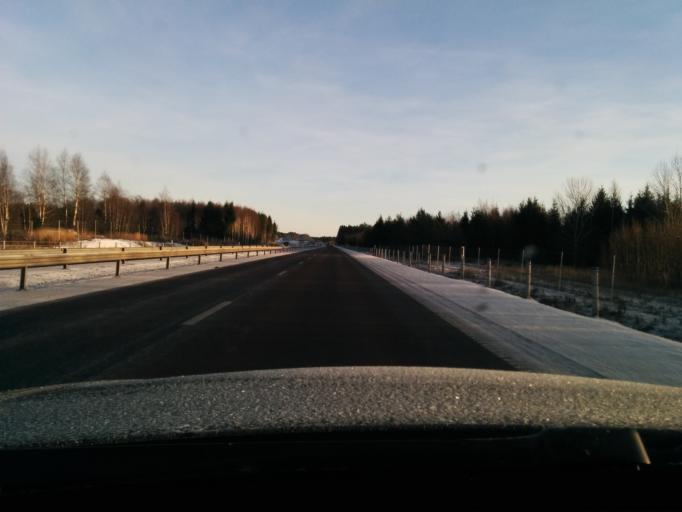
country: SE
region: Vaestmanland
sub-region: Vasteras
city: Tillberga
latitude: 59.6245
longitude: 16.7426
